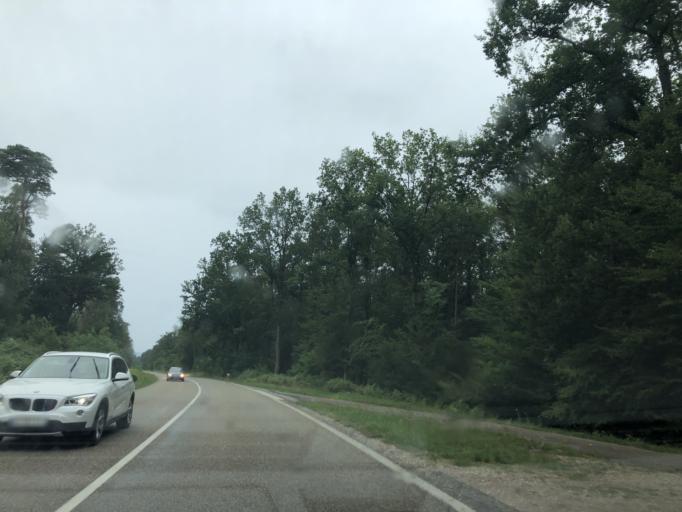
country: DE
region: Rheinland-Pfalz
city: Steinfeld
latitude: 49.0014
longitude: 8.0620
